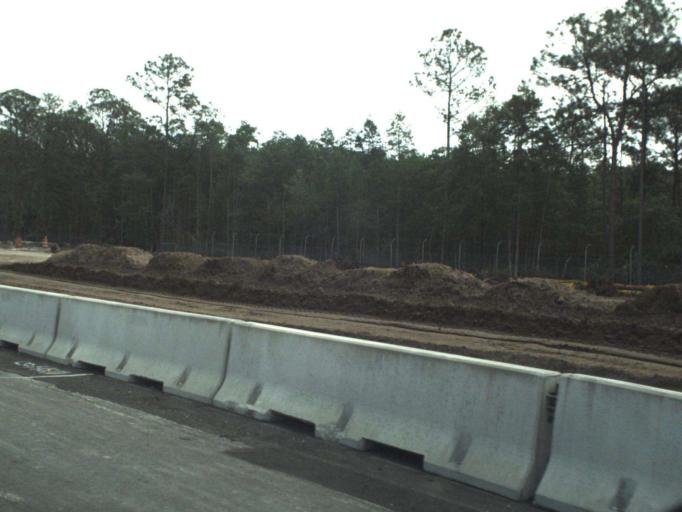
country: US
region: Florida
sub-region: Volusia County
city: Samsula-Spruce Creek
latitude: 29.1020
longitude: -81.1519
